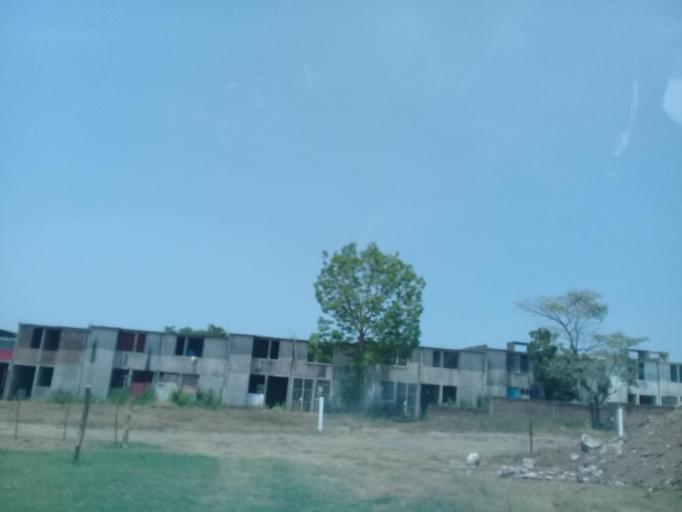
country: MX
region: Veracruz
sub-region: Veracruz
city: Las Amapolas
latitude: 19.1591
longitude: -96.2160
